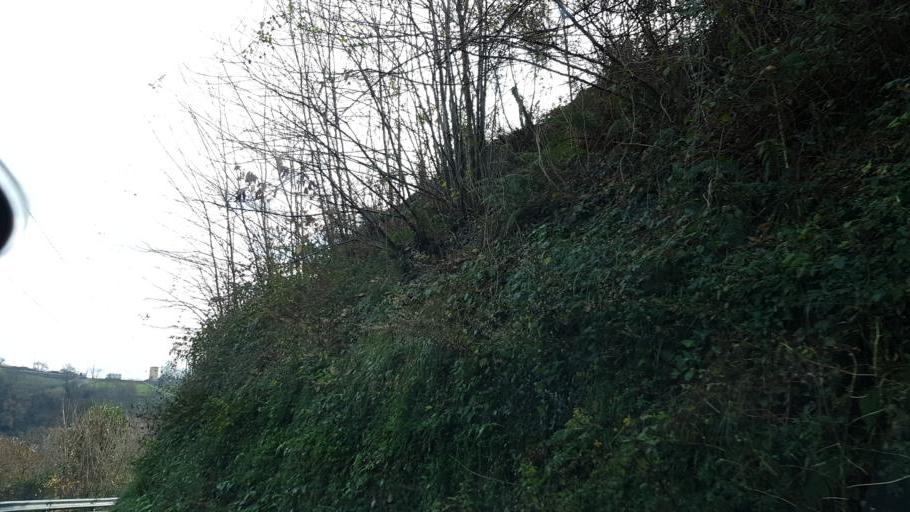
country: IT
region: Liguria
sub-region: Provincia di Genova
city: Santa Marta
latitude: 44.4852
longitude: 8.8860
